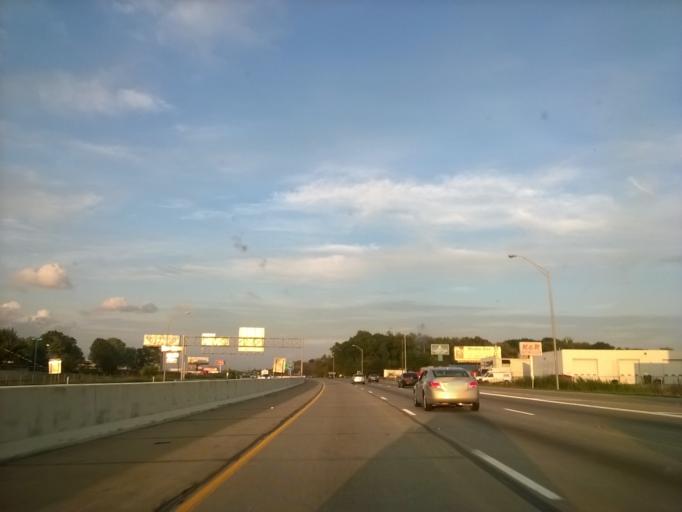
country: US
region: Indiana
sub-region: Marion County
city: Beech Grove
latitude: 39.7035
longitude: -86.0770
